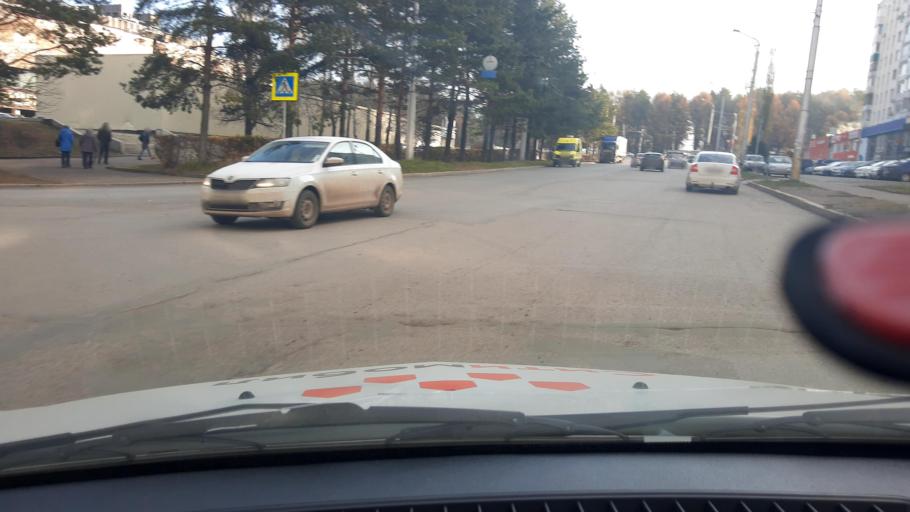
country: RU
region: Bashkortostan
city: Ufa
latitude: 54.7404
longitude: 56.0248
